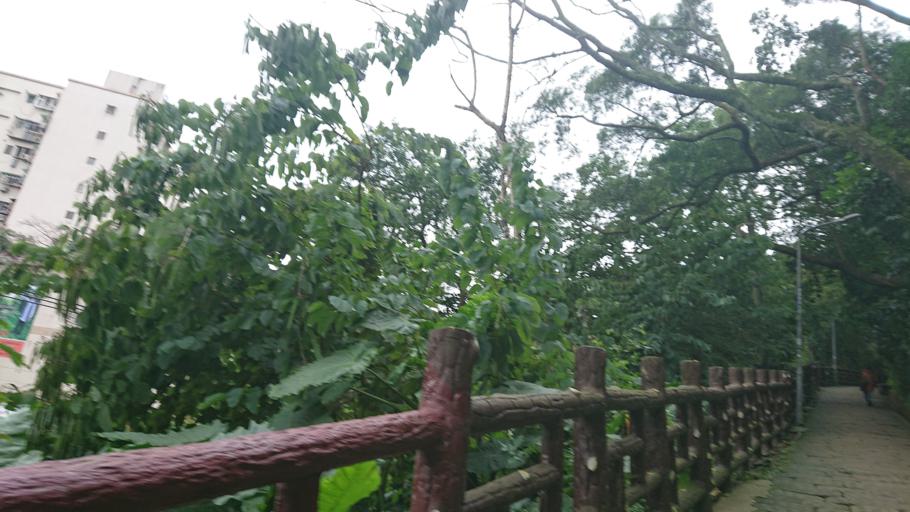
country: TW
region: Taipei
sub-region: Taipei
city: Banqiao
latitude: 24.9584
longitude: 121.4444
